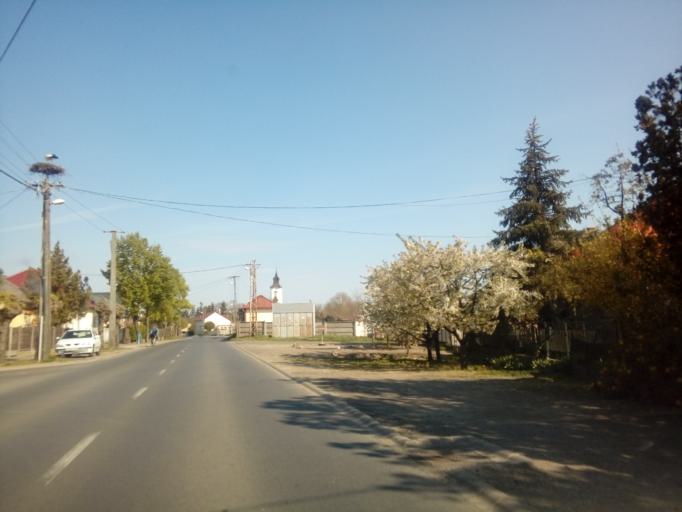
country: HU
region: Szabolcs-Szatmar-Bereg
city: Nagykallo
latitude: 47.8695
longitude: 21.8476
